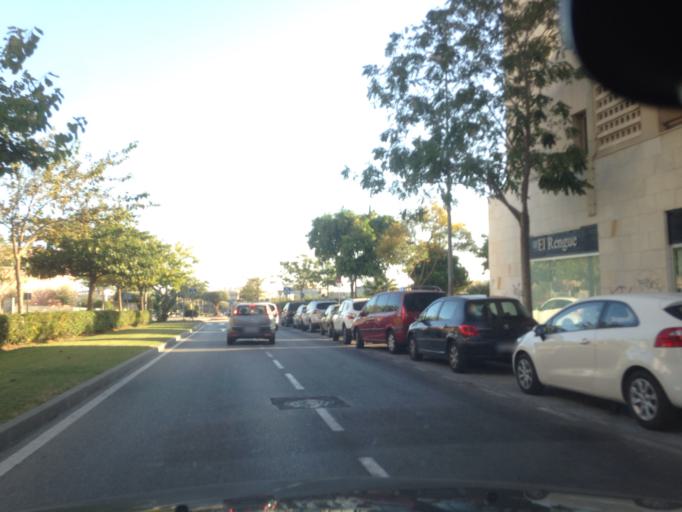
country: ES
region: Andalusia
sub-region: Provincia de Malaga
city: Malaga
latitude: 36.7157
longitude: -4.4635
